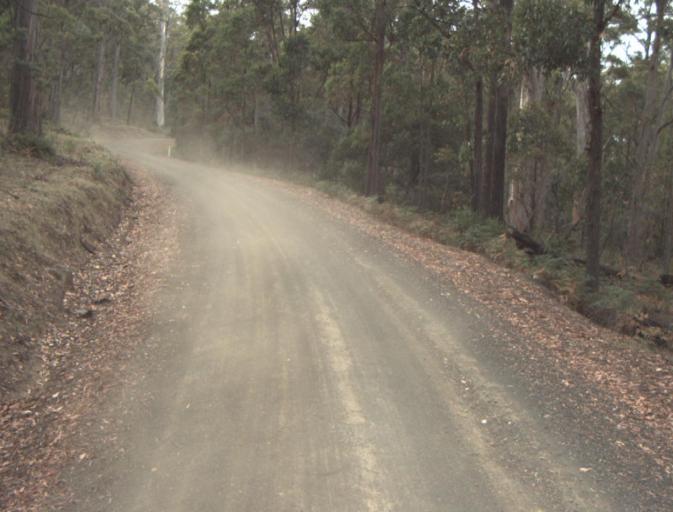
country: AU
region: Tasmania
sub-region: Northern Midlands
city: Evandale
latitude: -41.4911
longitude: 147.5464
